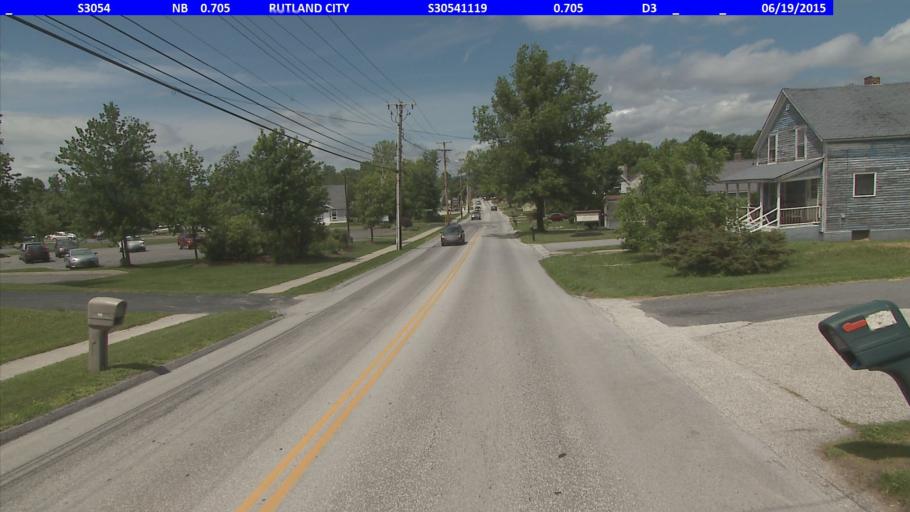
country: US
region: Vermont
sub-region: Rutland County
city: Rutland
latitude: 43.6016
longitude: -72.9558
